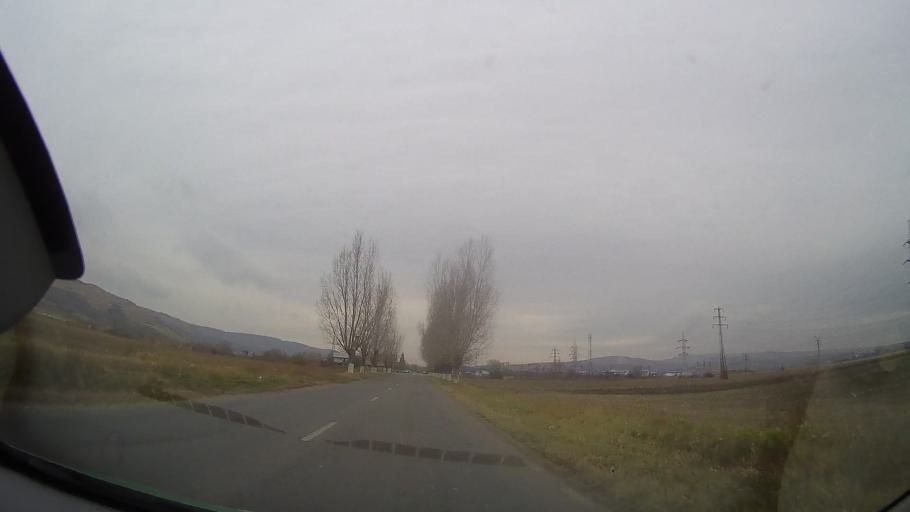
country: RO
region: Prahova
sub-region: Oras Urlati
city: Urlati
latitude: 44.9697
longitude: 26.2339
